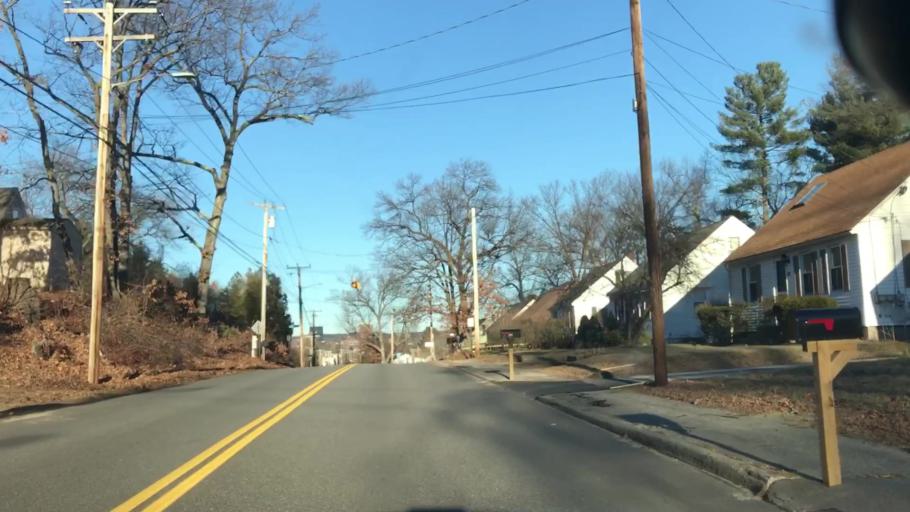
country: US
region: New Hampshire
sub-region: Hillsborough County
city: Pinardville
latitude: 42.9704
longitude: -71.4861
